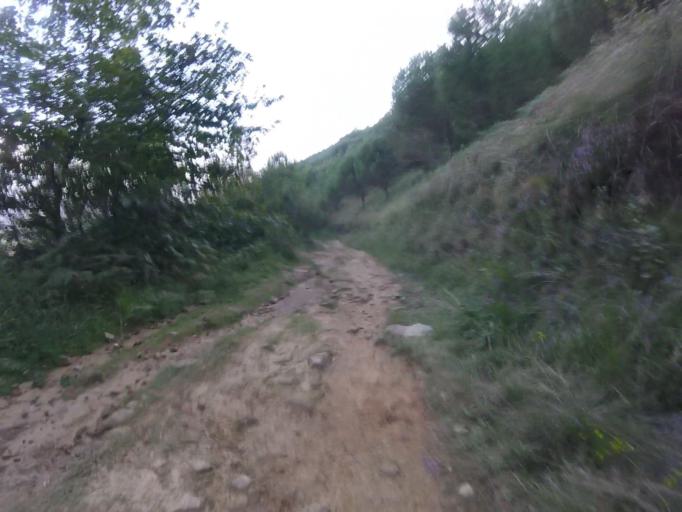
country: ES
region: Basque Country
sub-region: Provincia de Guipuzcoa
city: Fuenterrabia
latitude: 43.3551
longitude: -1.8375
